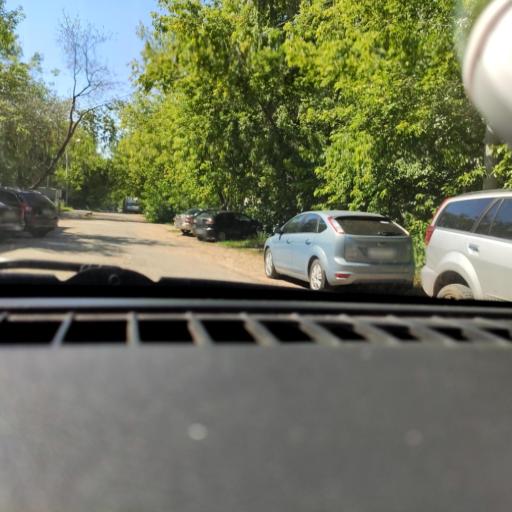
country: RU
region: Perm
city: Polazna
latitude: 58.1256
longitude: 56.3793
